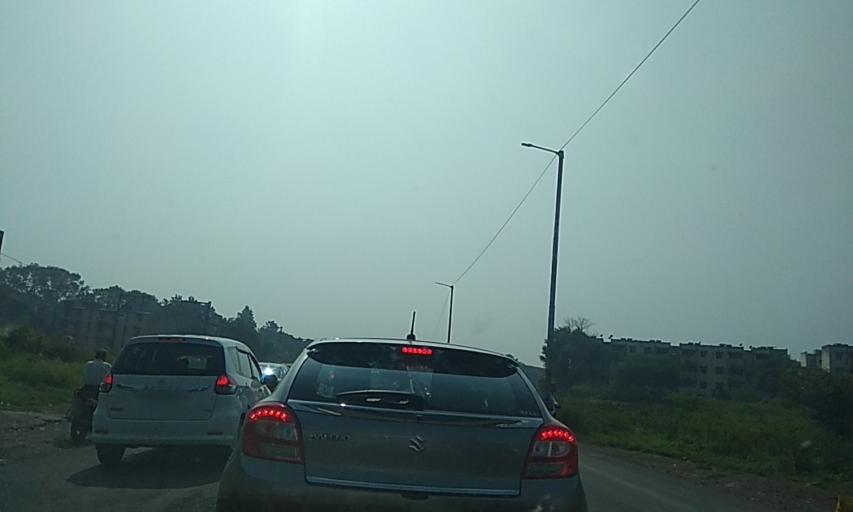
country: IN
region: Maharashtra
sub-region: Pune Division
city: Khadki
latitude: 18.5583
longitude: 73.8436
